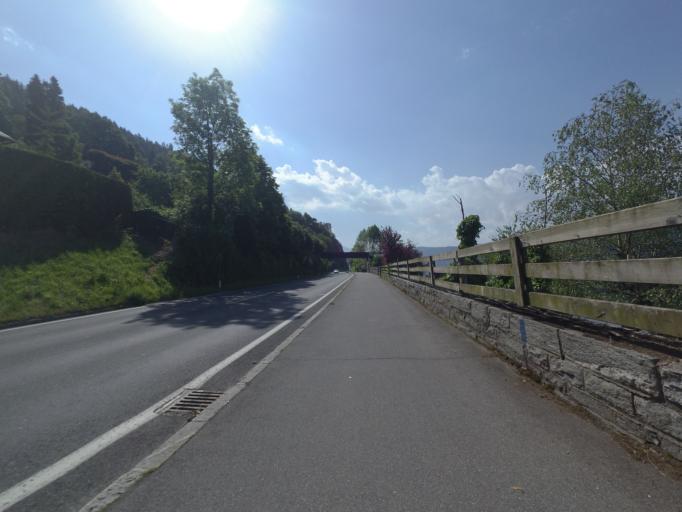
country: AT
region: Carinthia
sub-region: Politischer Bezirk Spittal an der Drau
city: Millstatt
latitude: 46.8012
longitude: 13.5810
